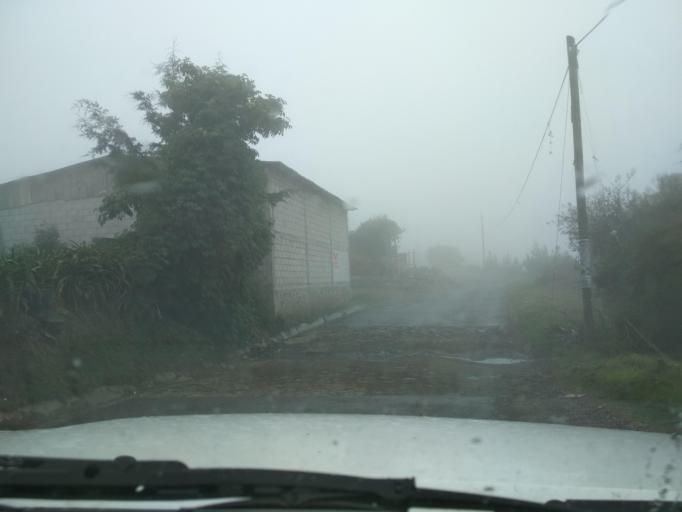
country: MX
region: Veracruz
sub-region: Mariano Escobedo
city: San Isidro el Berro
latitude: 18.9302
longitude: -97.2108
